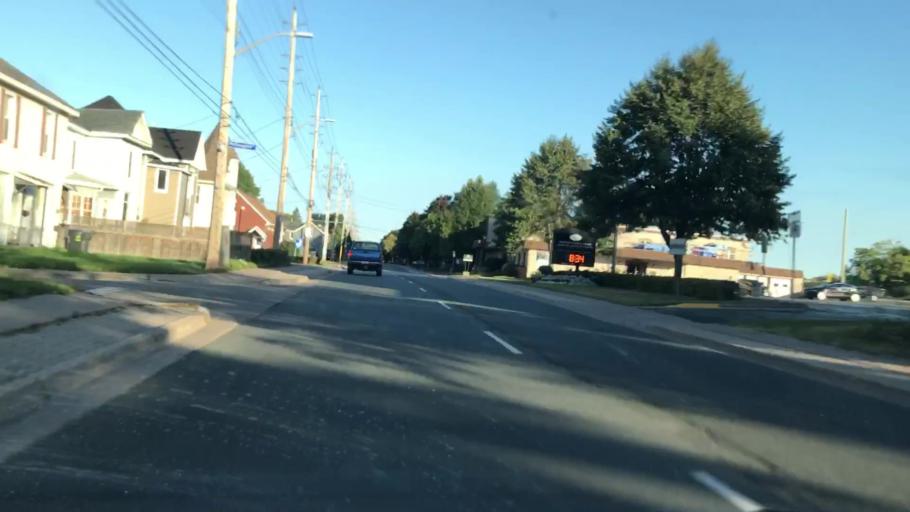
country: CA
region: Ontario
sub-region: Algoma
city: Sault Ste. Marie
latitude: 46.5113
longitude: -84.3278
